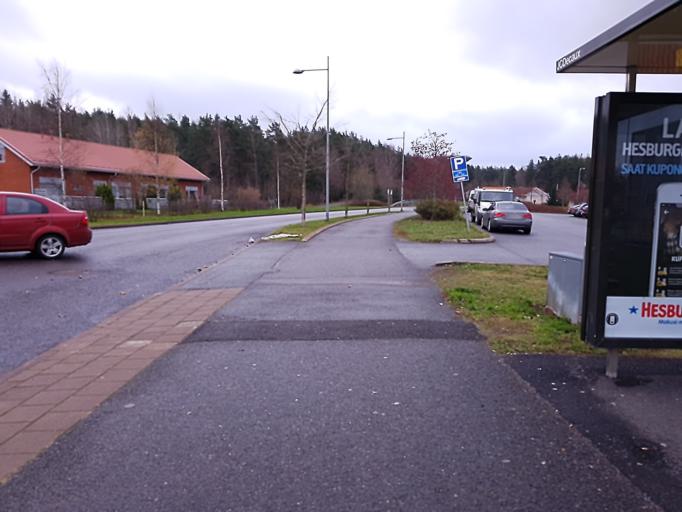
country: FI
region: Varsinais-Suomi
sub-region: Turku
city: Rusko
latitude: 60.4923
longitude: 22.2408
